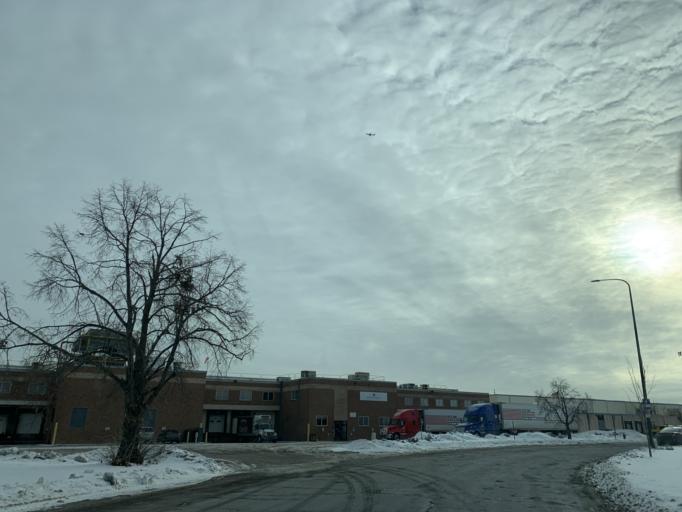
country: US
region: Minnesota
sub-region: Ramsey County
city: Saint Paul
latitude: 44.9409
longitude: -93.0729
